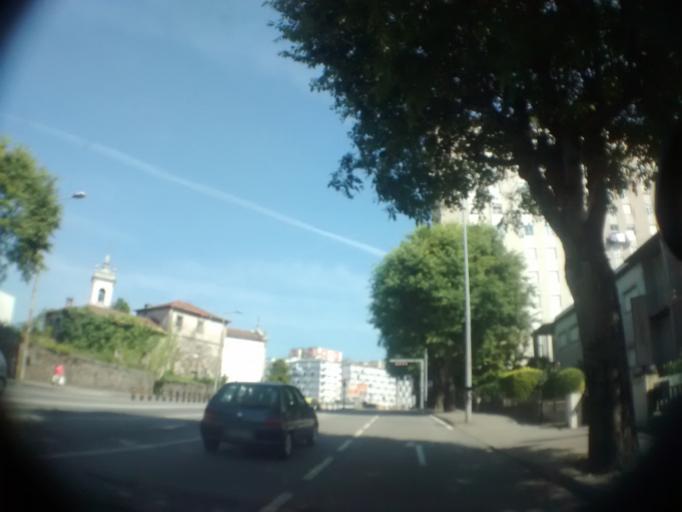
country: PT
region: Braga
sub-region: Braga
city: Braga
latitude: 41.5435
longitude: -8.4324
